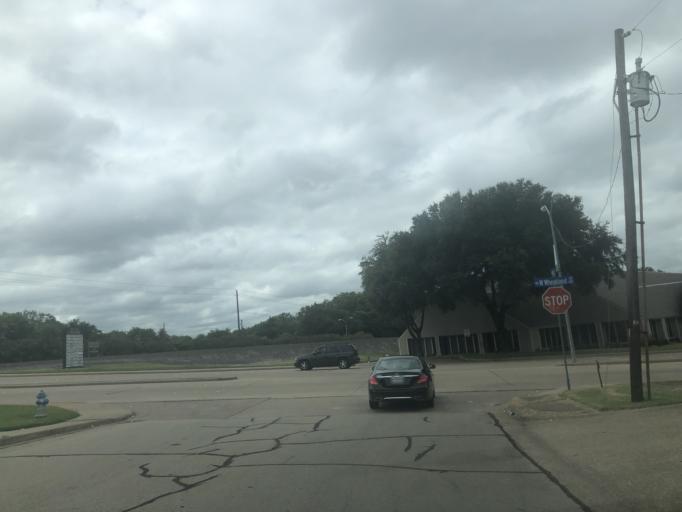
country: US
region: Texas
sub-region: Dallas County
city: Duncanville
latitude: 32.6463
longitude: -96.9162
